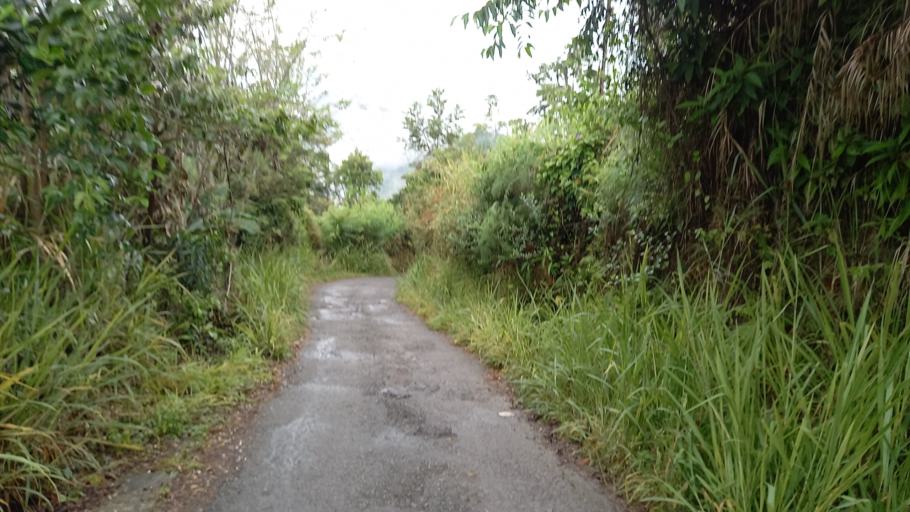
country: CO
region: Antioquia
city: Santa Barbara
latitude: 5.8458
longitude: -75.5753
